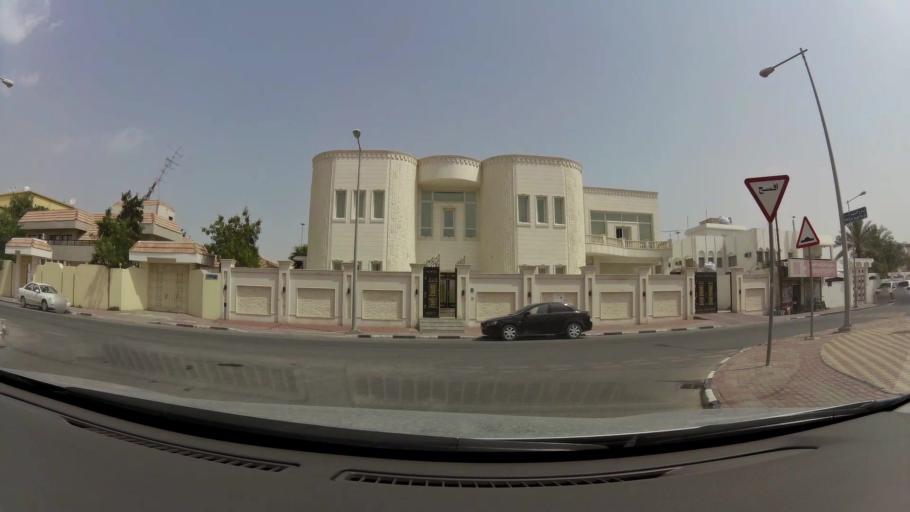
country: QA
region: Baladiyat ar Rayyan
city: Ar Rayyan
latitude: 25.2332
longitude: 51.4298
